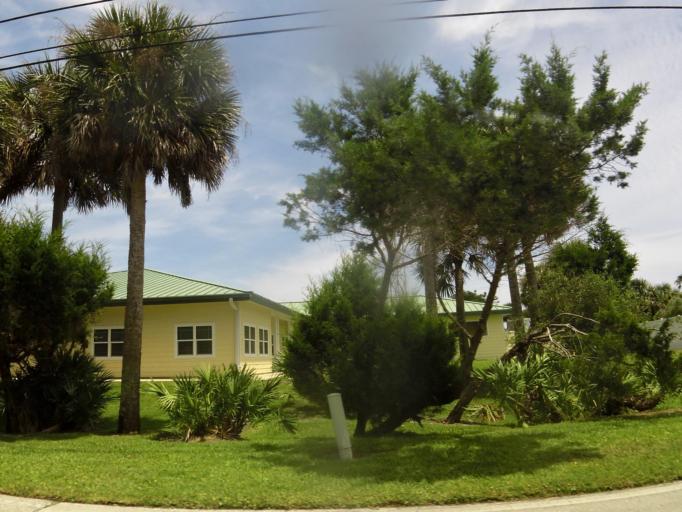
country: US
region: Florida
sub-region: Volusia County
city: Ponce Inlet
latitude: 29.1203
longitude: -80.9537
